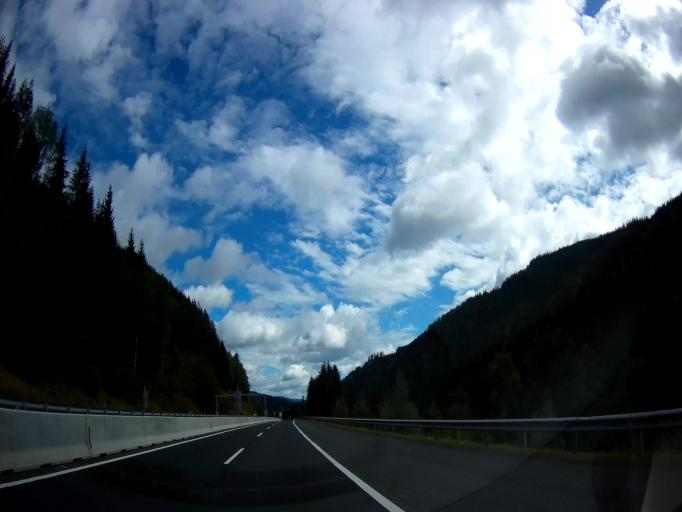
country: AT
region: Styria
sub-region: Politischer Bezirk Graz-Umgebung
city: Ubelbach
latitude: 47.2472
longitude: 15.1631
